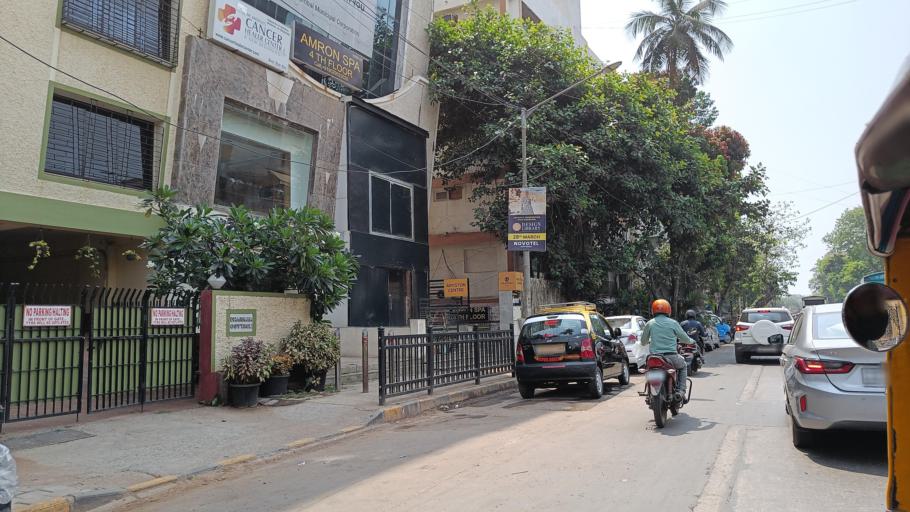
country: IN
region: Maharashtra
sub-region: Mumbai Suburban
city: Mumbai
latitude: 19.1018
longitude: 72.8271
